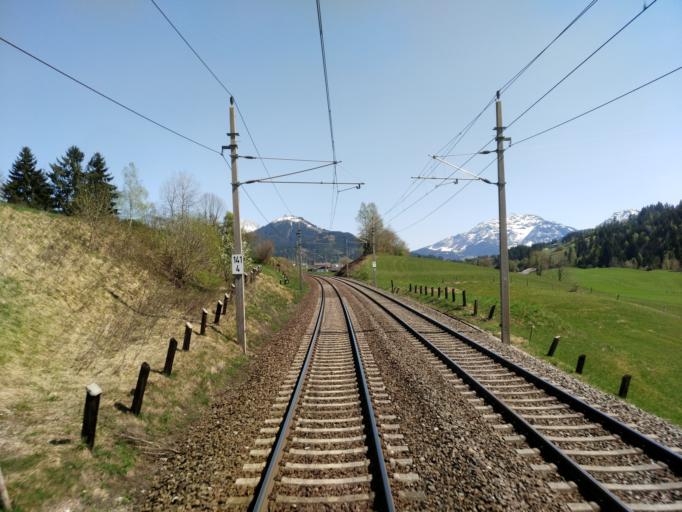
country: AT
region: Tyrol
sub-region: Politischer Bezirk Kitzbuhel
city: Fieberbrunn
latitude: 47.4962
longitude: 12.5035
